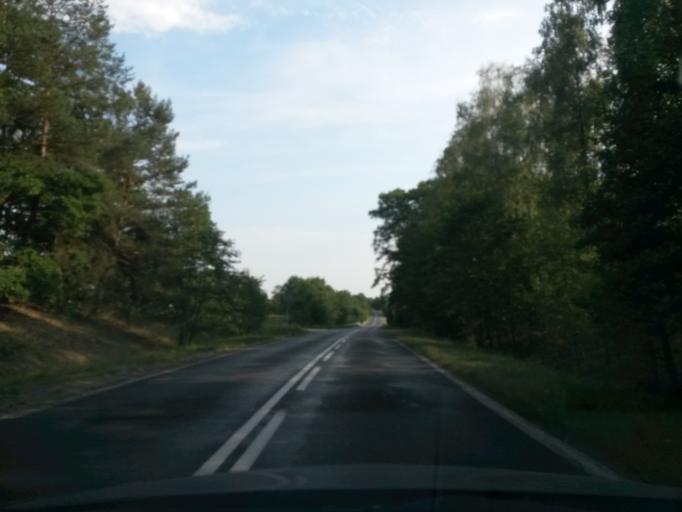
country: PL
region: Masovian Voivodeship
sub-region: Powiat sierpecki
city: Sierpc
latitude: 52.8909
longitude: 19.6523
